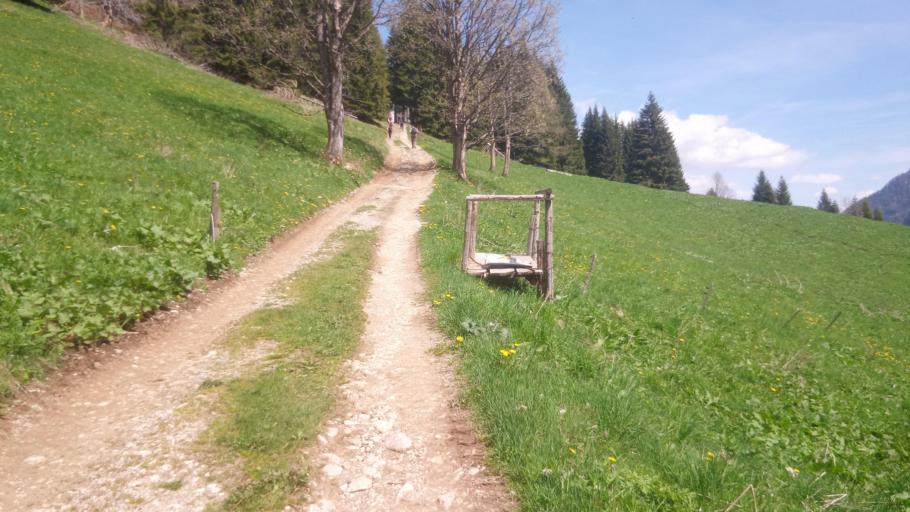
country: IT
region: Veneto
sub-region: Provincia di Belluno
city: Pie' Falcade
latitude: 46.3141
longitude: 11.8799
